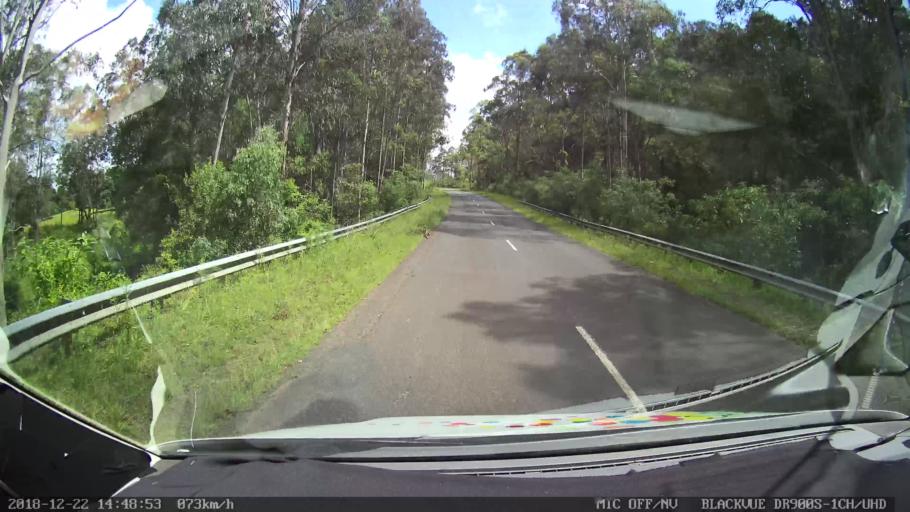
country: AU
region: New South Wales
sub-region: Bellingen
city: Dorrigo
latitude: -30.1846
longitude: 152.5513
